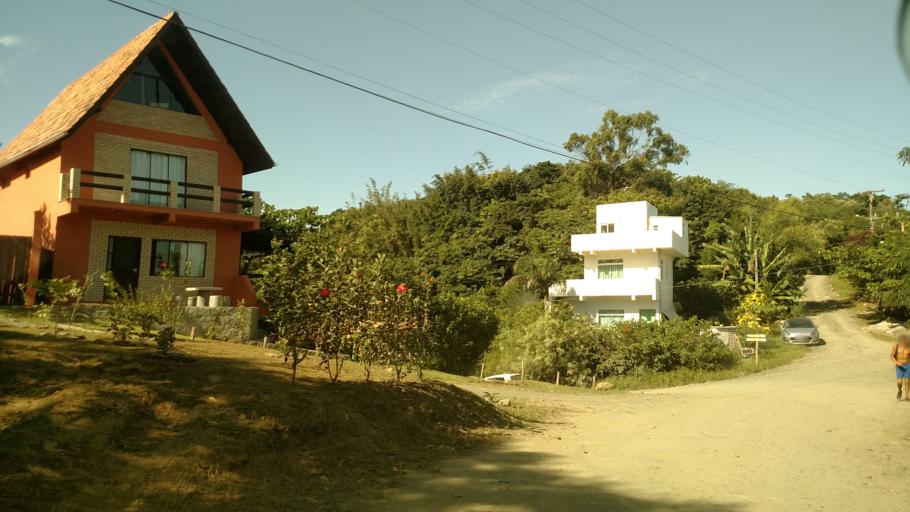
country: BR
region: Santa Catarina
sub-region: Porto Belo
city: Porto Belo
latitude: -27.2136
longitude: -48.5098
